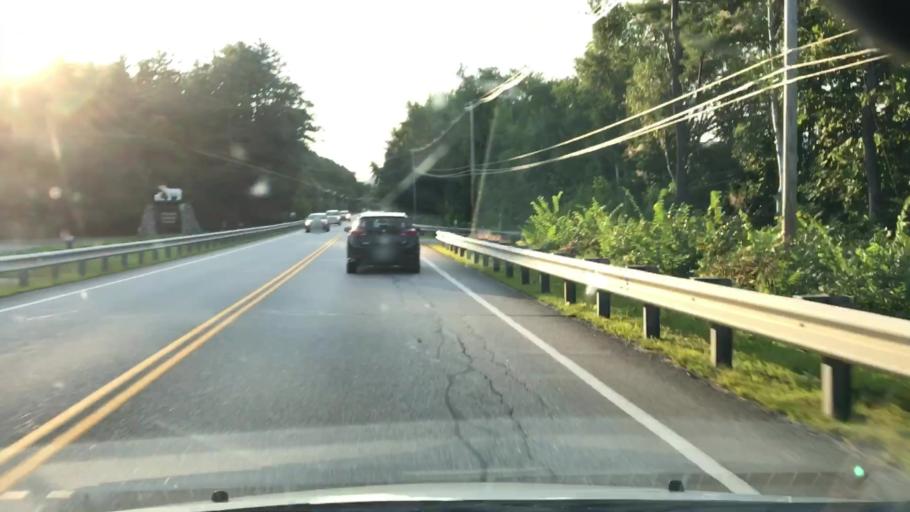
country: US
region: New Hampshire
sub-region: Grafton County
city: Rumney
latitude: 43.7819
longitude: -71.7790
